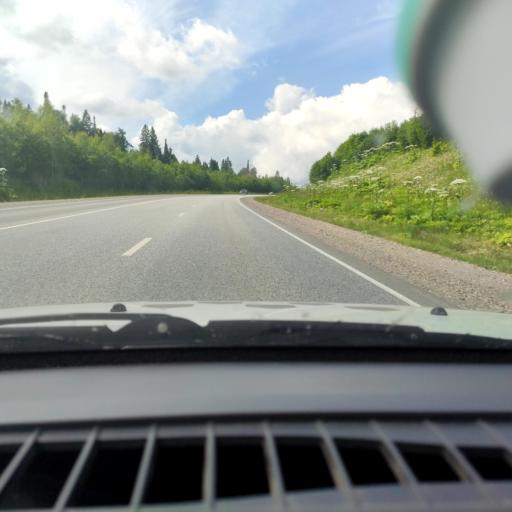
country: RU
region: Perm
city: Polazna
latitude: 58.2903
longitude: 56.4934
